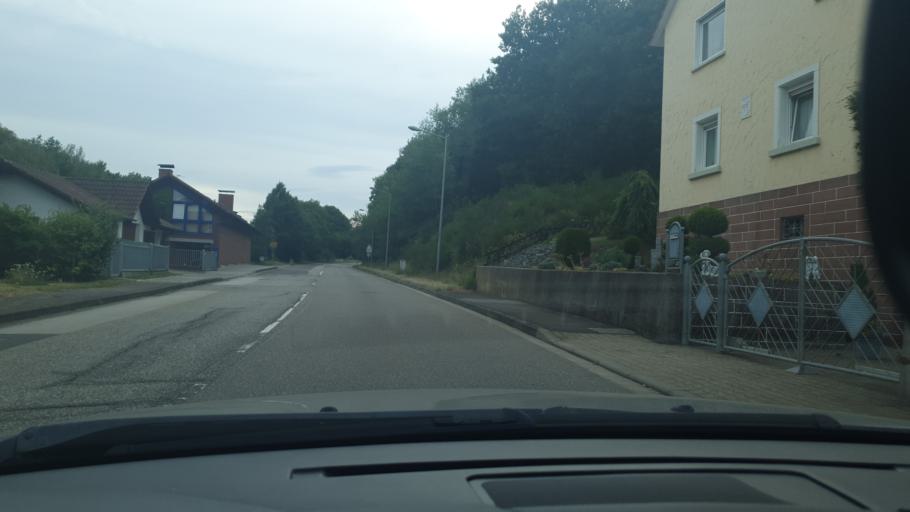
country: DE
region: Rheinland-Pfalz
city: Hochspeyer
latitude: 49.4433
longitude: 7.8815
